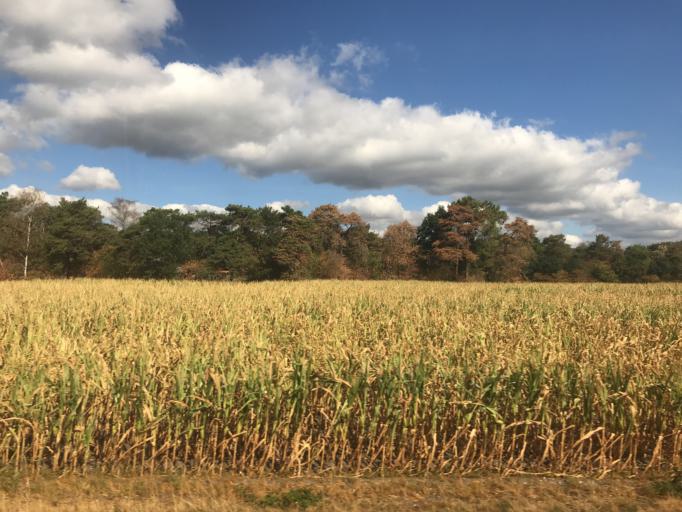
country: NL
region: Overijssel
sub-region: Gemeente Hof van Twente
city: Markelo
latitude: 52.2916
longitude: 6.4601
